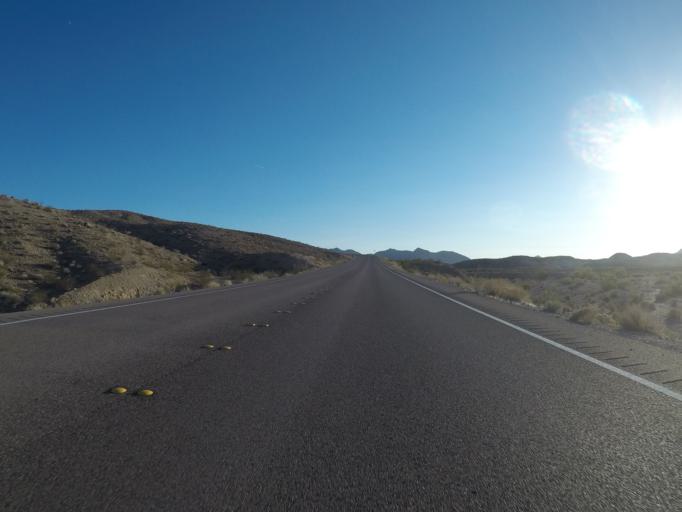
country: US
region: Nevada
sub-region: Clark County
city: Moapa Valley
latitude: 36.3068
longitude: -114.4893
